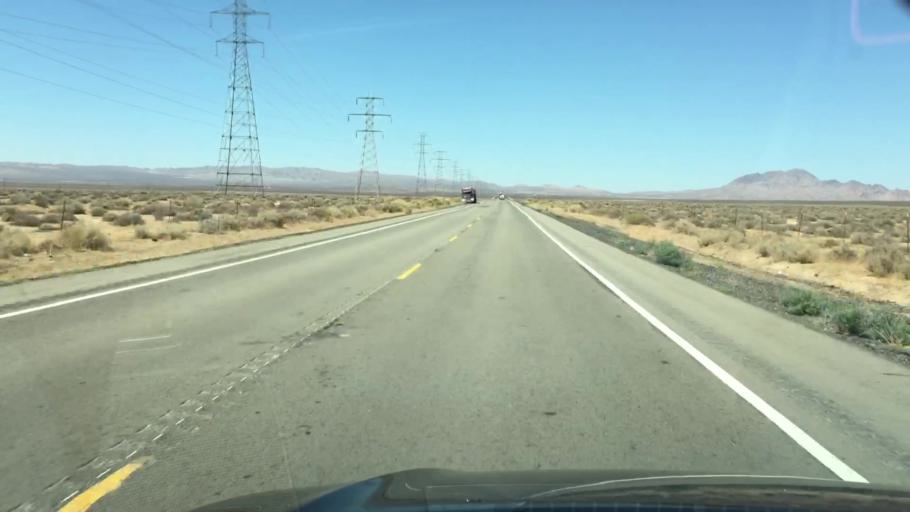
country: US
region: California
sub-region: Kern County
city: Boron
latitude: 35.1927
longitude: -117.5974
